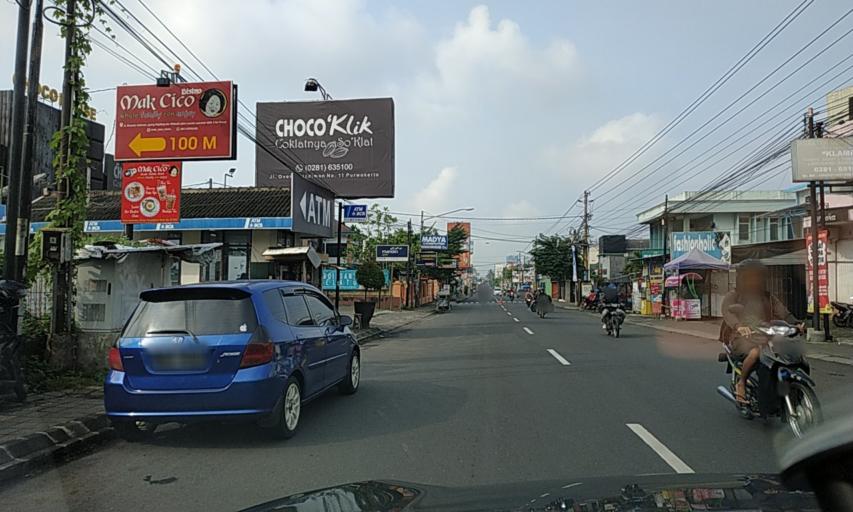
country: ID
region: Central Java
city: Purwokerto
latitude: -7.4202
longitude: 109.2443
